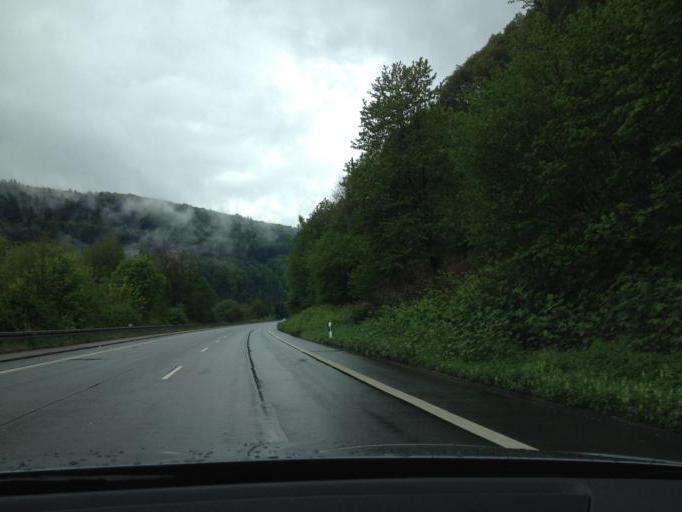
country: DE
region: Hesse
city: Neckarsteinach
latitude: 49.3990
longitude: 8.8222
